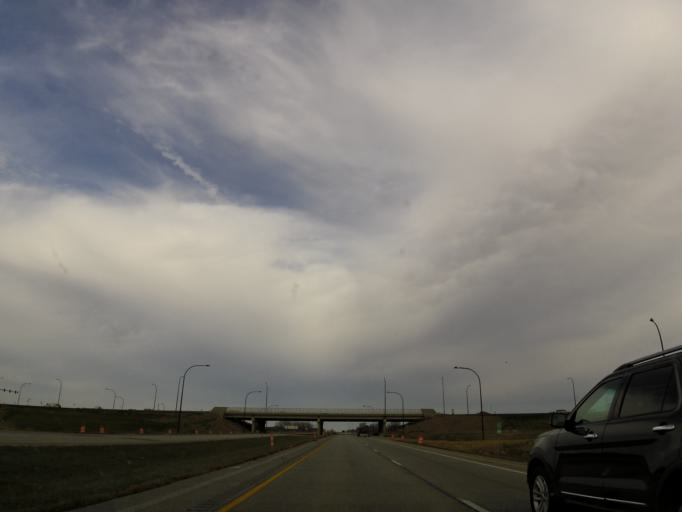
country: US
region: Iowa
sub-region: Scott County
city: Bettendorf
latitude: 41.5728
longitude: -90.5222
